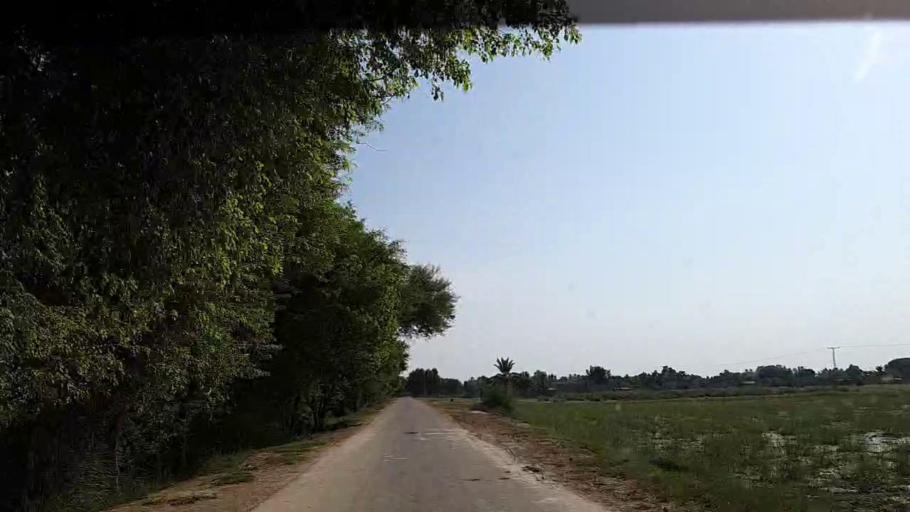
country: PK
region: Sindh
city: Adilpur
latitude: 27.9251
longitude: 69.2498
